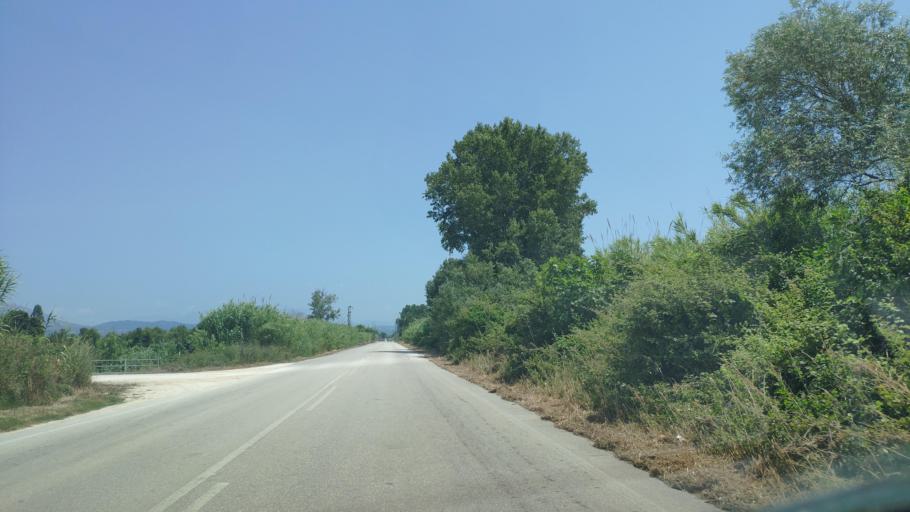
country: GR
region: Epirus
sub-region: Nomos Artas
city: Aneza
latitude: 39.0976
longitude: 20.9095
